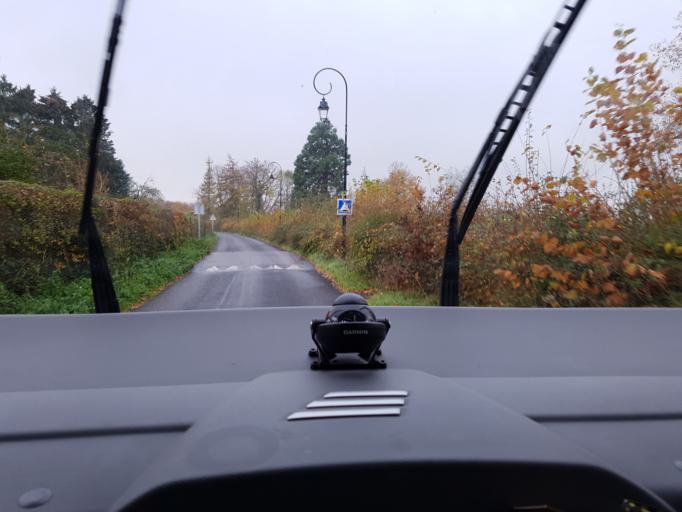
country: FR
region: Haute-Normandie
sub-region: Departement de la Seine-Maritime
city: Petiville
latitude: 49.4299
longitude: 0.6254
